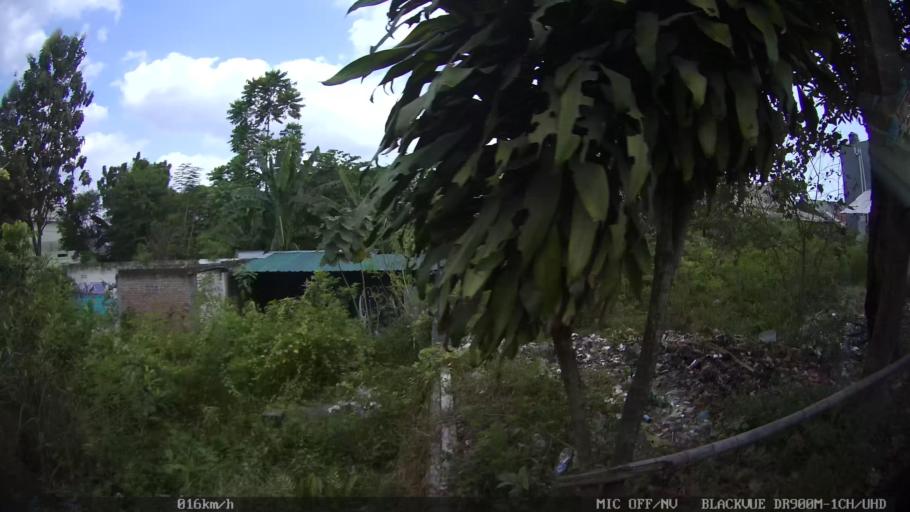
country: ID
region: Daerah Istimewa Yogyakarta
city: Kasihan
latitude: -7.8112
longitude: 110.3442
